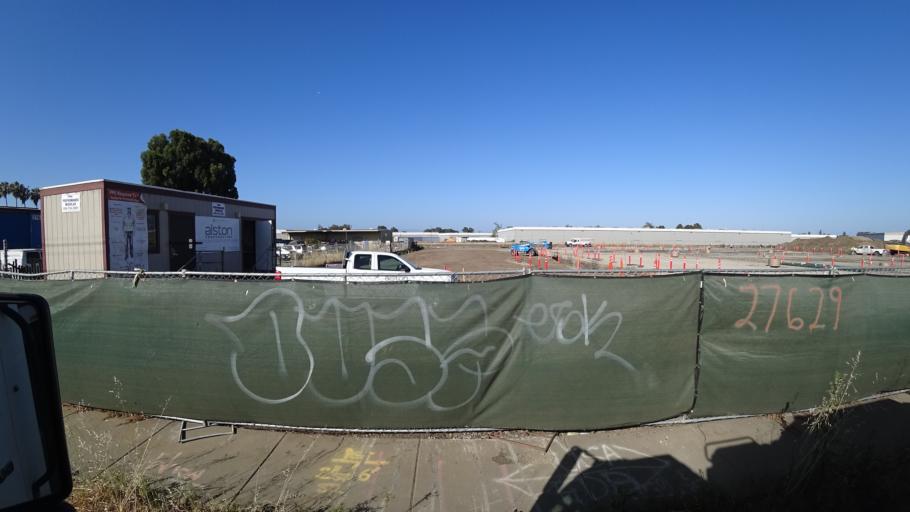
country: US
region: California
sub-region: Alameda County
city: Hayward
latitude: 37.6235
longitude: -122.1030
